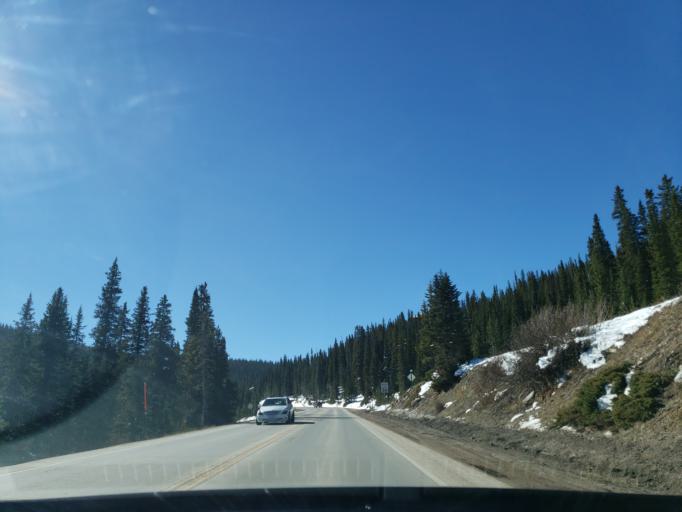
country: US
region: Colorado
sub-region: Summit County
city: Breckenridge
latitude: 39.3776
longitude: -106.0573
